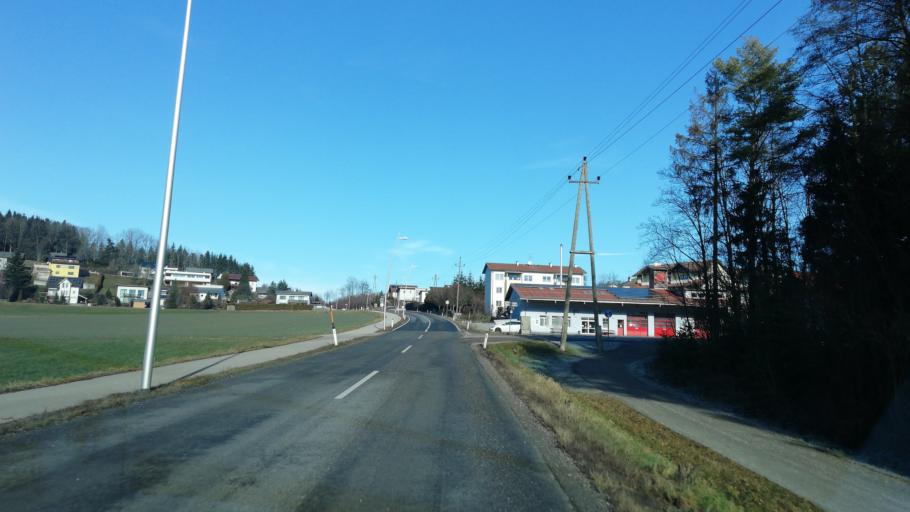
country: AT
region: Upper Austria
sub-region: Politischer Bezirk Ried im Innkreis
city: Ried im Innkreis
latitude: 48.1806
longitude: 13.5765
